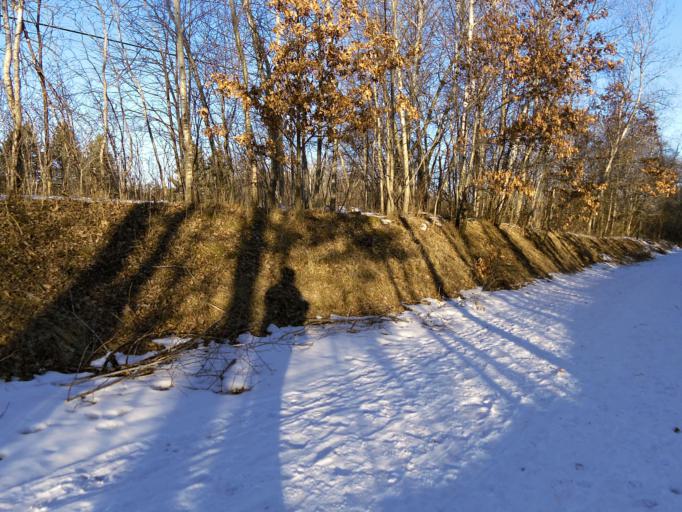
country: US
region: Minnesota
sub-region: Washington County
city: Stillwater
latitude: 45.0720
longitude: -92.8540
